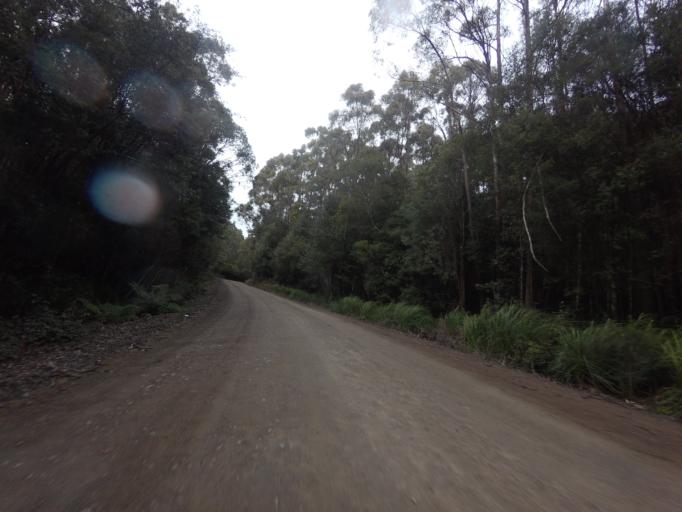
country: AU
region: Tasmania
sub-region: Huon Valley
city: Geeveston
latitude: -43.5228
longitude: 146.8818
